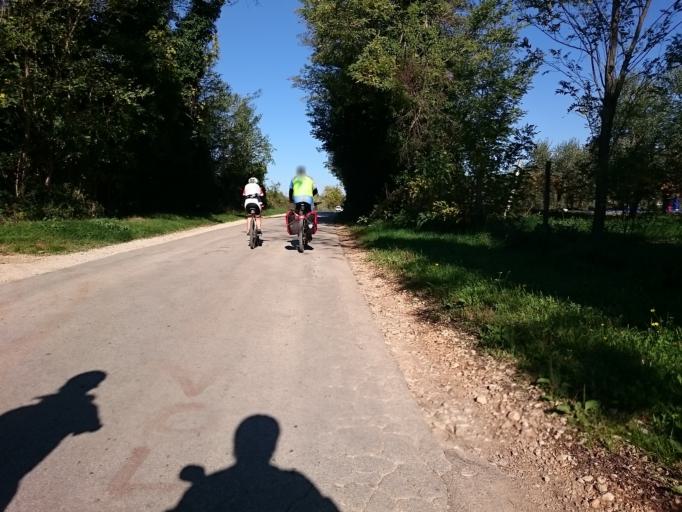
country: HR
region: Istarska
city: Umag
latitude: 45.4442
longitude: 13.5341
